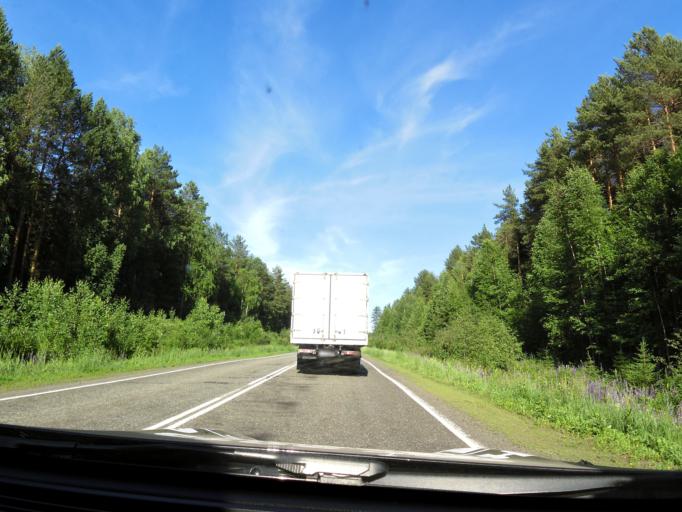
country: RU
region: Kirov
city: Dubrovka
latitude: 58.9050
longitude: 51.2115
